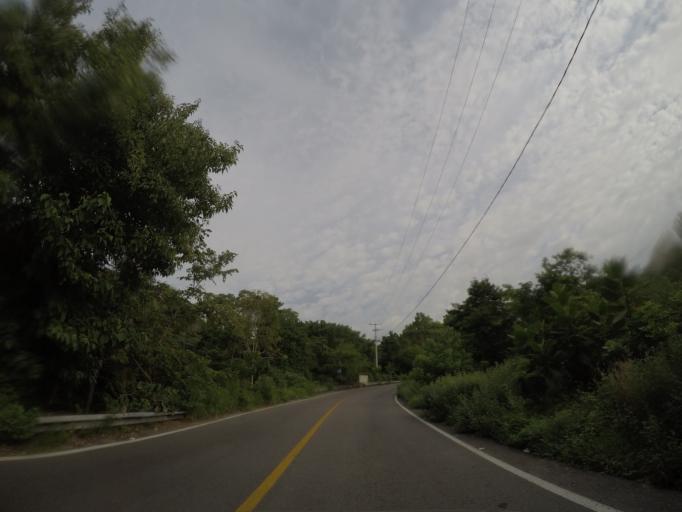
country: MX
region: Oaxaca
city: San Pedro Pochutla
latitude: 15.6992
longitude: -96.4827
